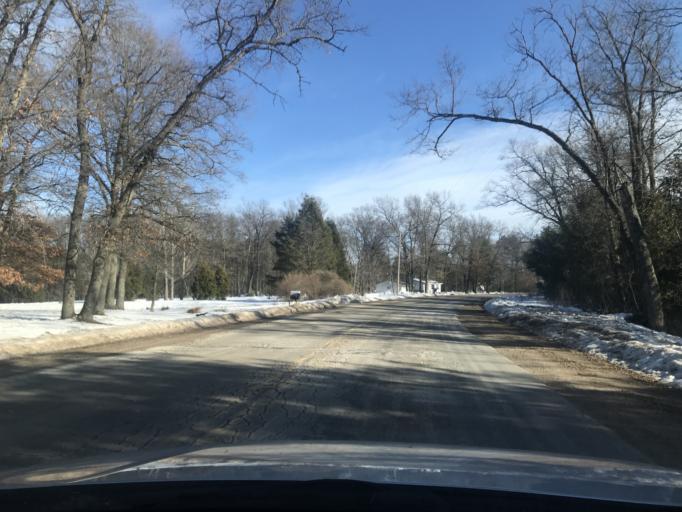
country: US
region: Wisconsin
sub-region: Marinette County
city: Peshtigo
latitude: 45.0312
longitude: -87.7126
